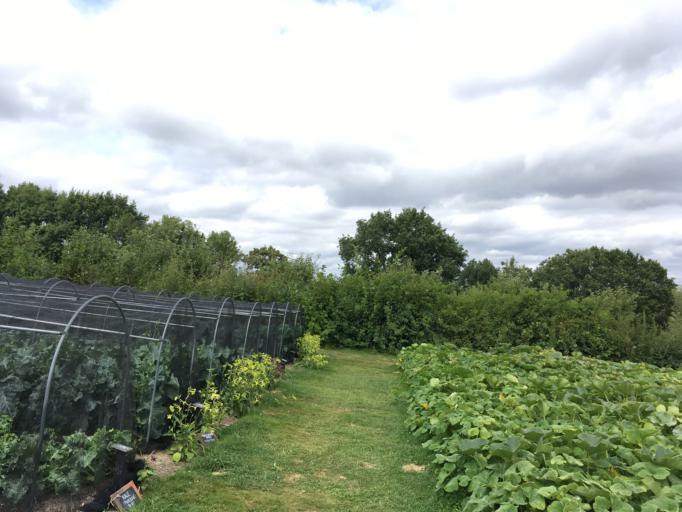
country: GB
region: England
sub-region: Kent
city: Cranbrook
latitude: 51.1174
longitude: 0.5801
